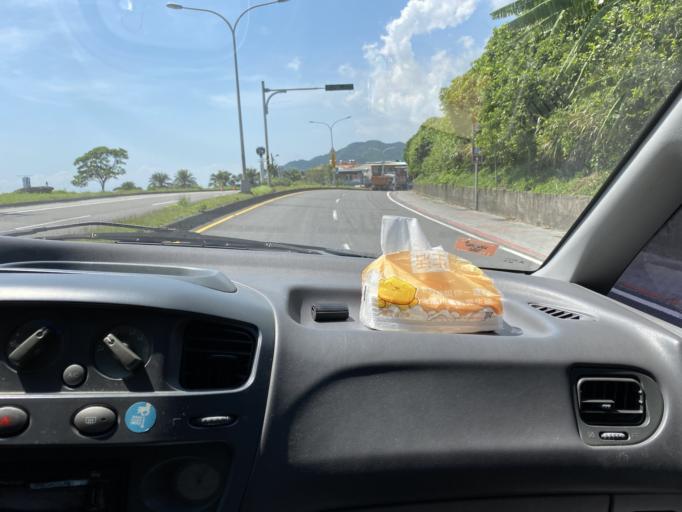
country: TW
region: Taiwan
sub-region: Yilan
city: Yilan
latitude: 24.9425
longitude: 121.9021
